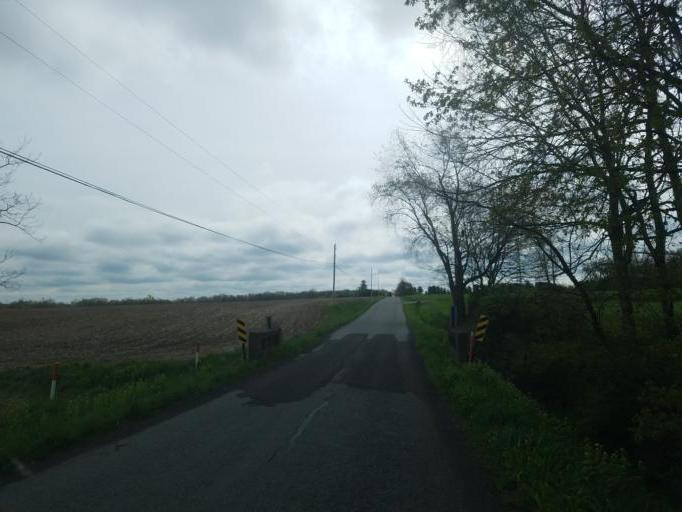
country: US
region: Ohio
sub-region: Wayne County
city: Apple Creek
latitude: 40.7480
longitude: -81.8950
